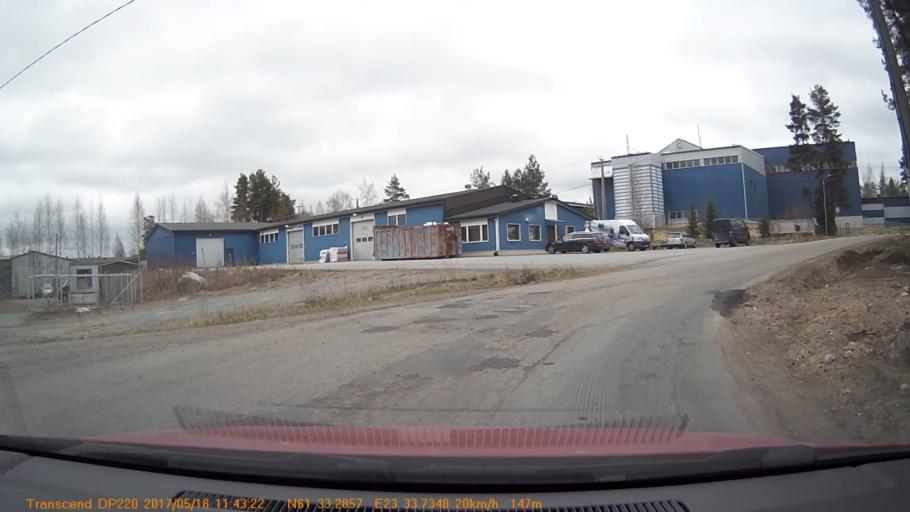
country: FI
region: Pirkanmaa
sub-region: Tampere
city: Yloejaervi
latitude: 61.5546
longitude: 23.5618
